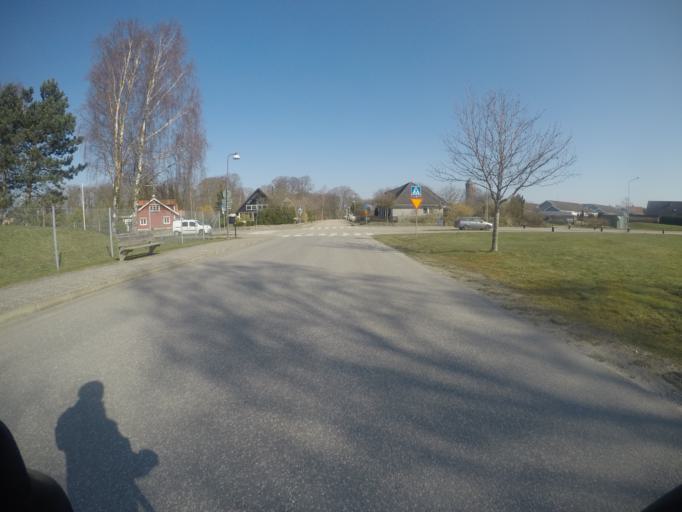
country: SE
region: Halland
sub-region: Laholms Kommun
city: Laholm
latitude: 56.5041
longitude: 13.0404
